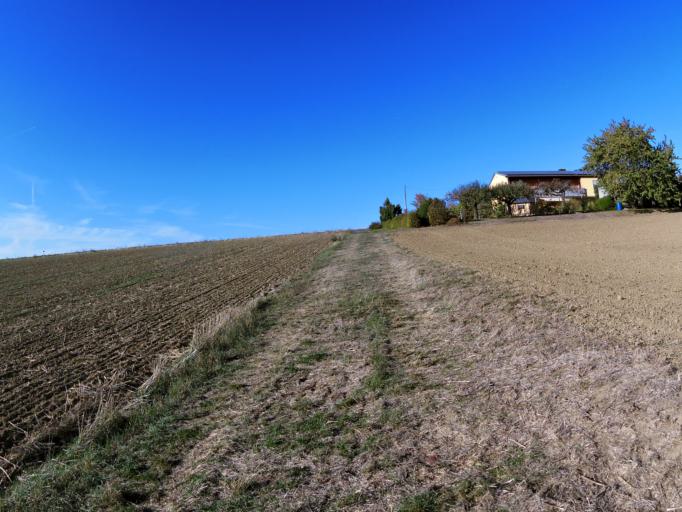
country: DE
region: Bavaria
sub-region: Regierungsbezirk Unterfranken
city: Reichenberg
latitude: 49.7129
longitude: 9.9344
